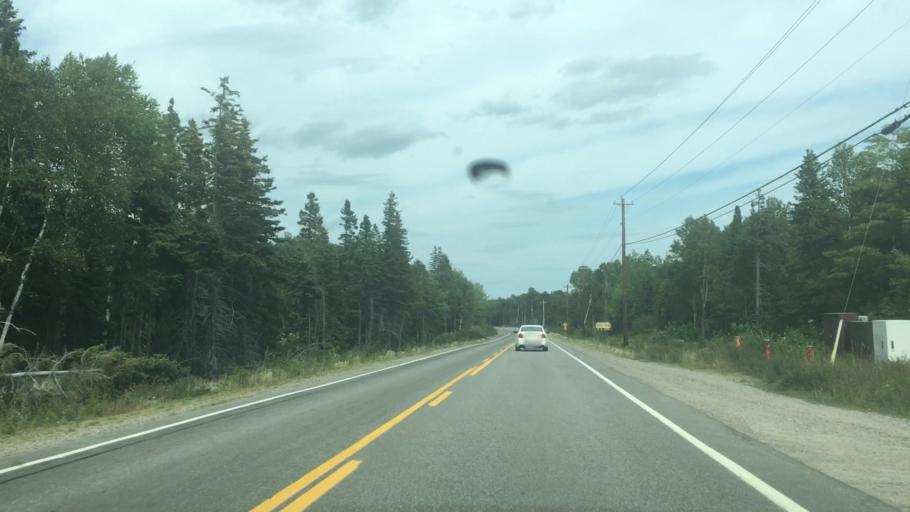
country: CA
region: Nova Scotia
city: Sydney Mines
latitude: 46.5066
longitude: -60.4332
